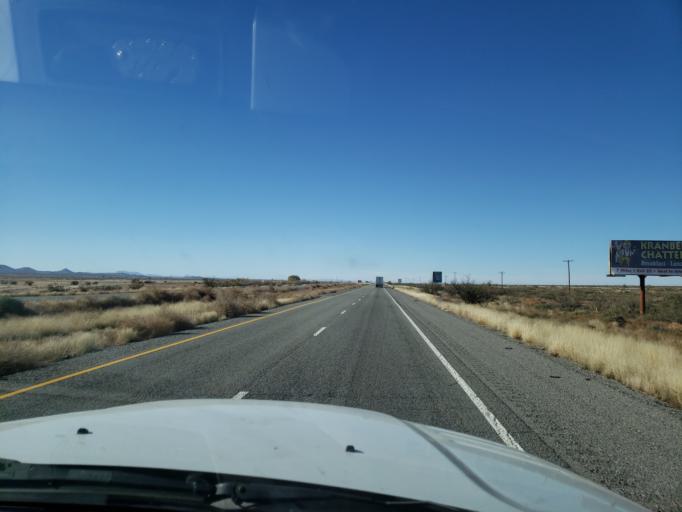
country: US
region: New Mexico
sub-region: Hidalgo County
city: Lordsburg
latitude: 32.3153
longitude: -108.6127
